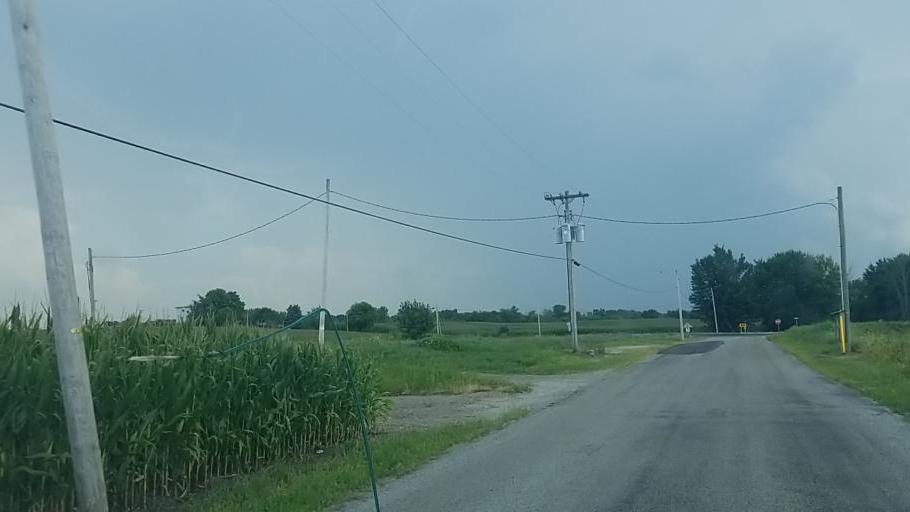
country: US
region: Ohio
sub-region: Medina County
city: Lodi
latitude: 41.0019
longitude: -82.0190
